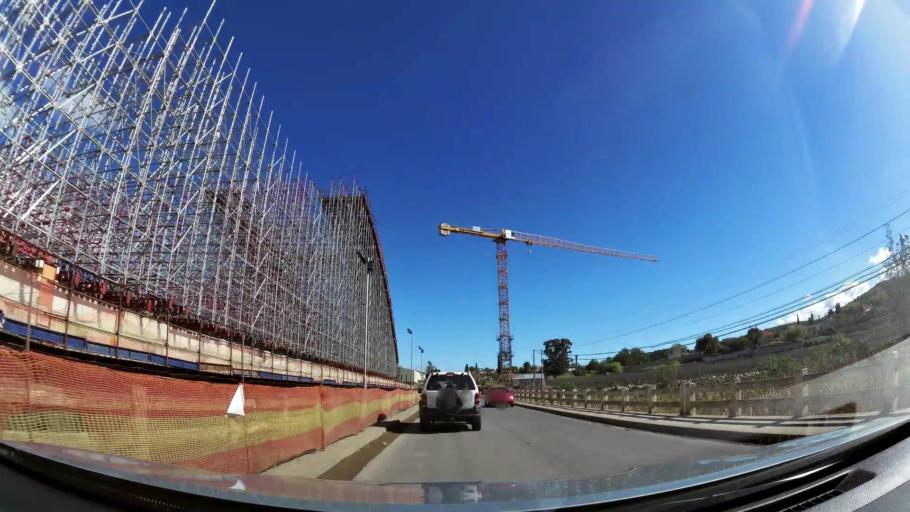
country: ZA
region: Western Cape
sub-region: Cape Winelands District Municipality
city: Ashton
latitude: -33.8337
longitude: 20.0603
